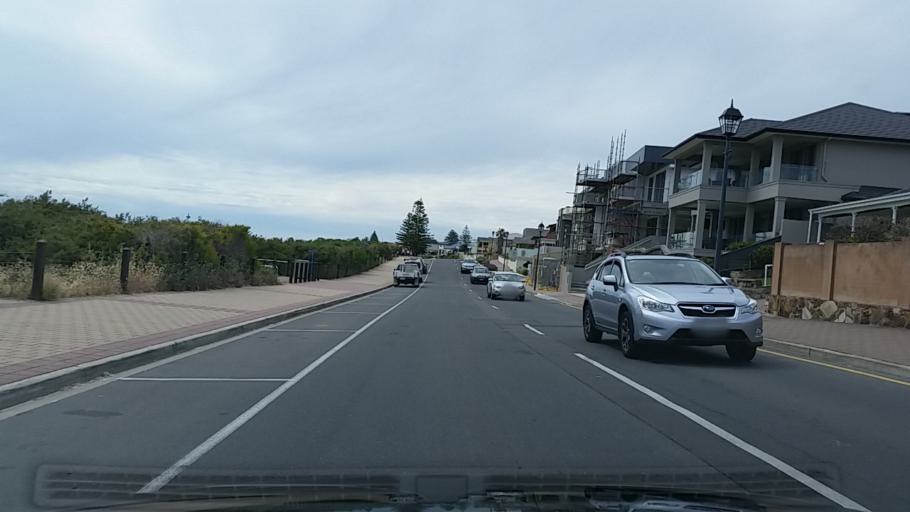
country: AU
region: South Australia
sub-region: Adelaide
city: Brighton
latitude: -35.0255
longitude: 138.5170
